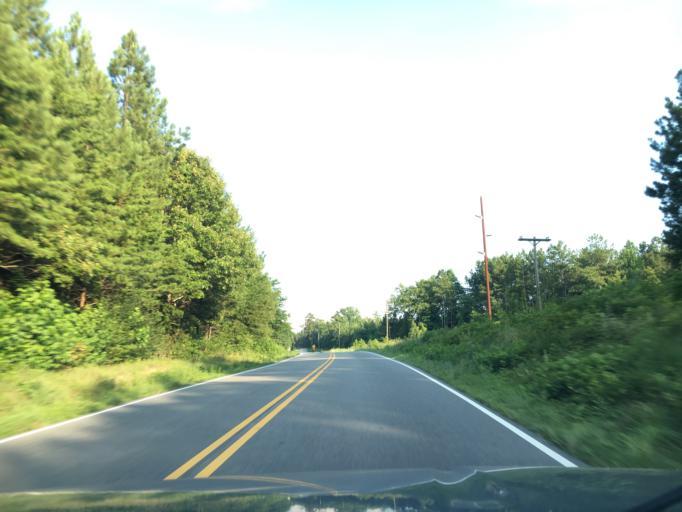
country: US
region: Virginia
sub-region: Pittsylvania County
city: Chatham
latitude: 36.8179
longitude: -79.2717
